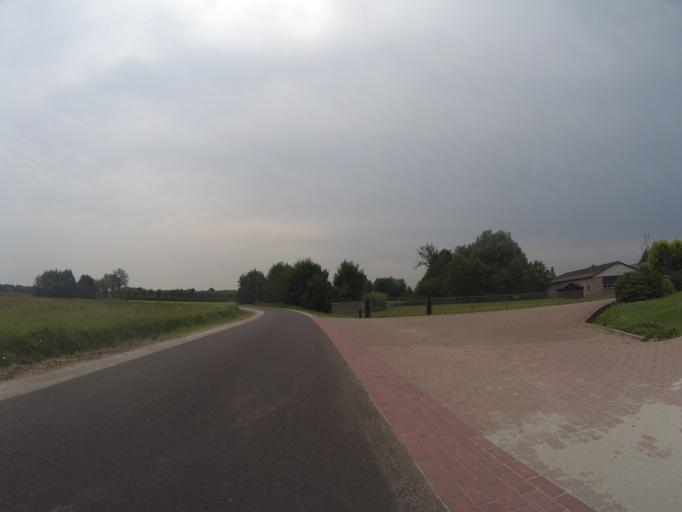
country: NL
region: Gelderland
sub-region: Gemeente Barneveld
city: Zwartebroek
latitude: 52.1895
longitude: 5.5001
